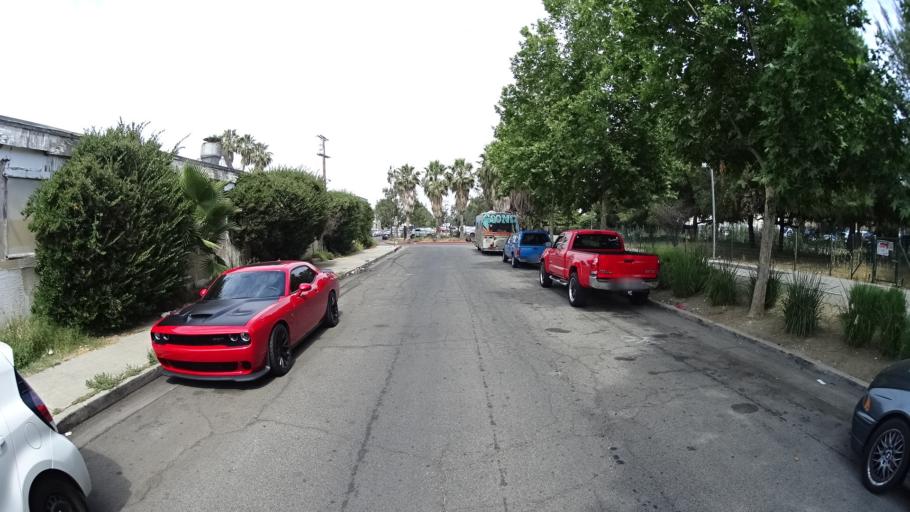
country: US
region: California
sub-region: Los Angeles County
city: Van Nuys
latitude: 34.1808
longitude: -118.4537
